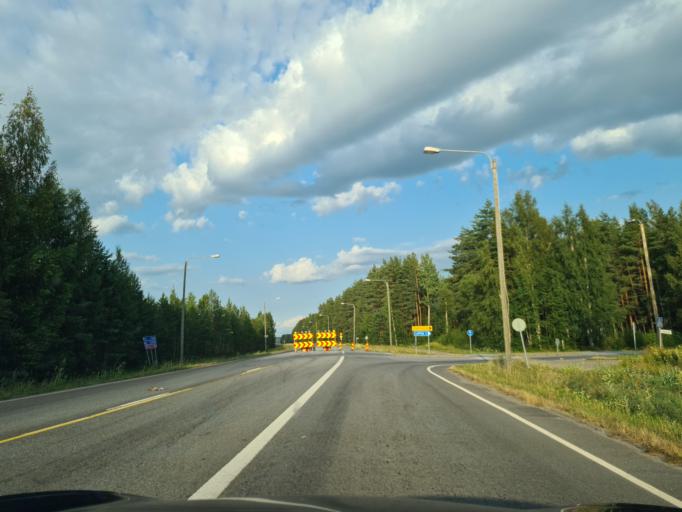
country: FI
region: Southern Ostrobothnia
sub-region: Seinaejoki
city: Lapua
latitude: 62.9865
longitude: 22.9384
